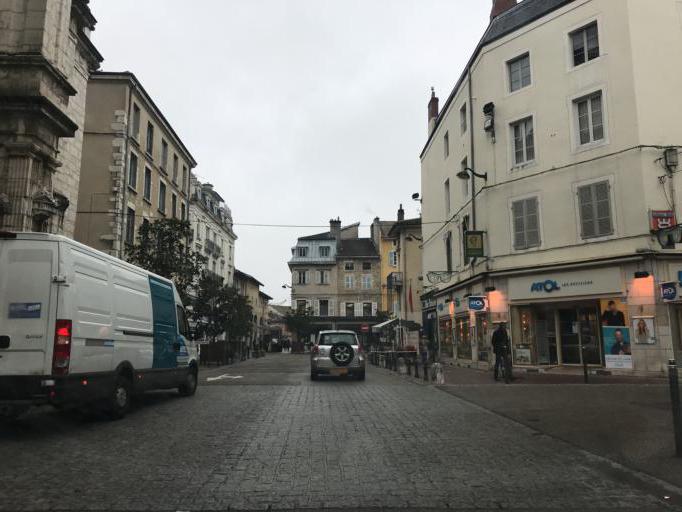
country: FR
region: Rhone-Alpes
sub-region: Departement de l'Ain
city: Bourg-en-Bresse
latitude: 46.2056
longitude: 5.2268
